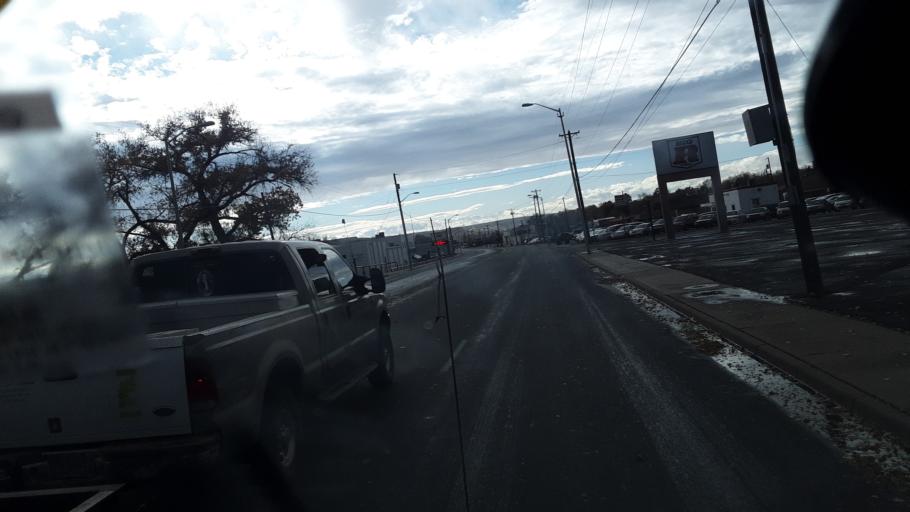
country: US
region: New Mexico
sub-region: San Juan County
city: Farmington
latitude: 36.7352
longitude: -108.1894
